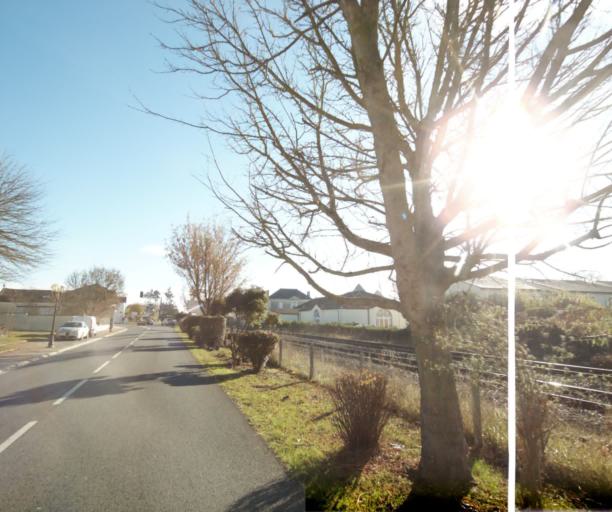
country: FR
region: Poitou-Charentes
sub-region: Departement de la Charente-Maritime
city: Chaniers
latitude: 45.7184
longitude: -0.5592
